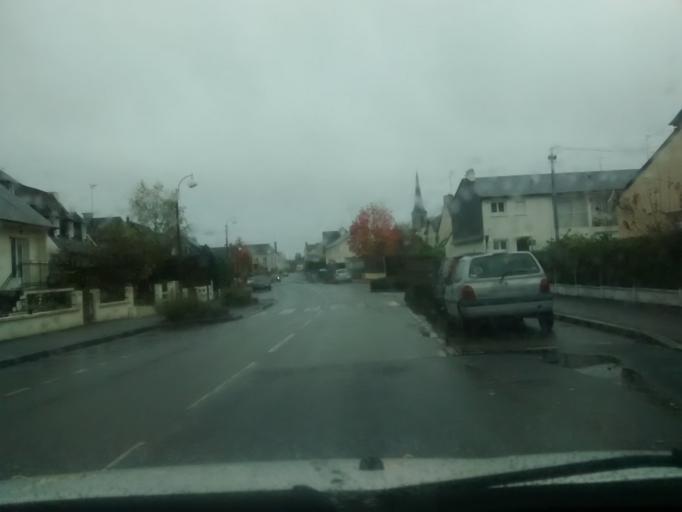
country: FR
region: Brittany
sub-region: Departement d'Ille-et-Vilaine
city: Chantepie
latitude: 48.0903
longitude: -1.6159
